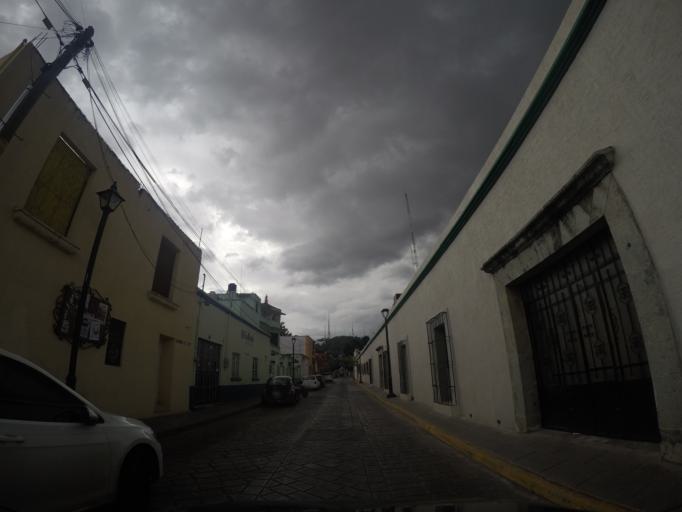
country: MX
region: Oaxaca
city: Oaxaca de Juarez
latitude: 17.0682
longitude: -96.7215
